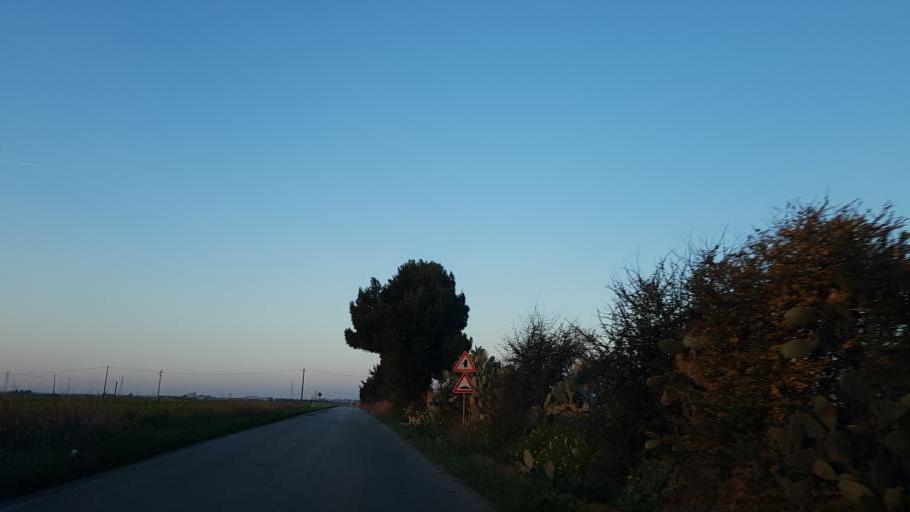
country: IT
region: Apulia
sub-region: Provincia di Brindisi
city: Tuturano
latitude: 40.5735
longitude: 17.9496
